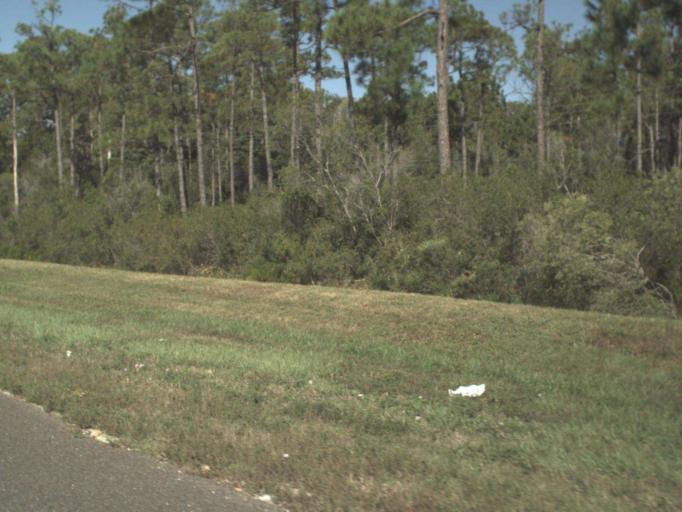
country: US
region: Florida
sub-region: Walton County
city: Seaside
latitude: 30.3578
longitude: -86.1468
